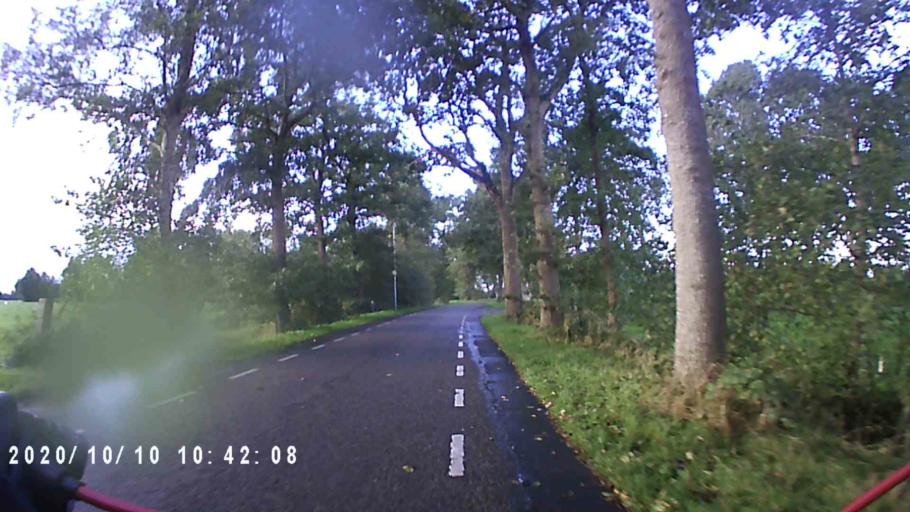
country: NL
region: Groningen
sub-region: Gemeente Grootegast
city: Grootegast
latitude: 53.1749
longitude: 6.2747
